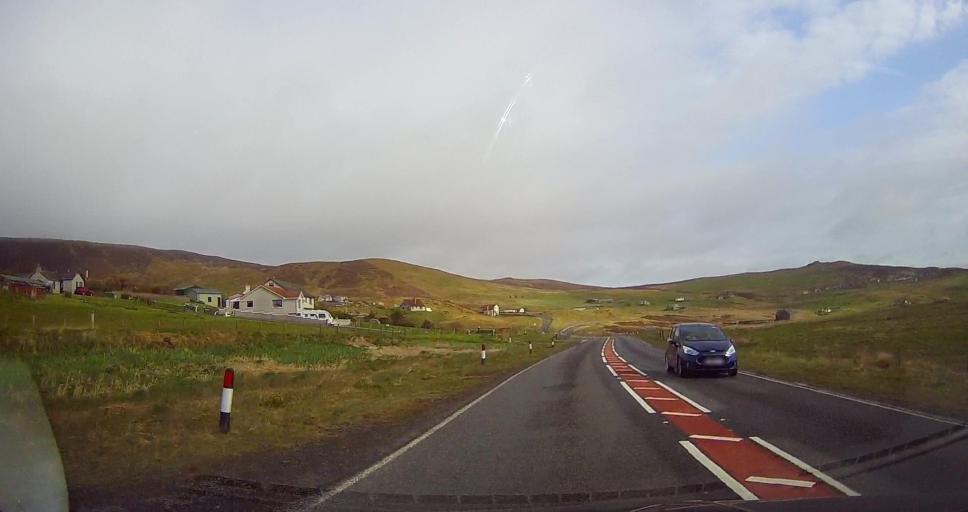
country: GB
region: Scotland
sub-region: Shetland Islands
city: Sandwick
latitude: 60.0972
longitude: -1.2337
